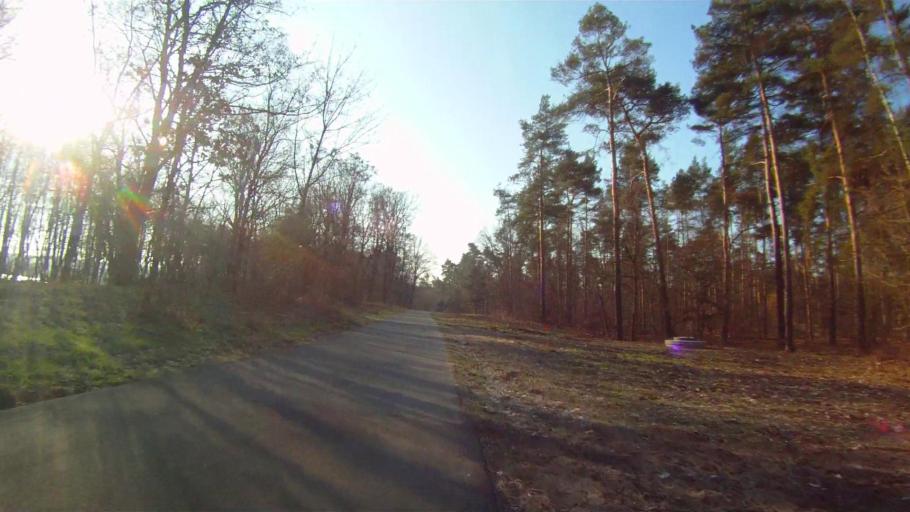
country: DE
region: Berlin
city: Friedrichshagen
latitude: 52.4347
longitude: 13.6196
